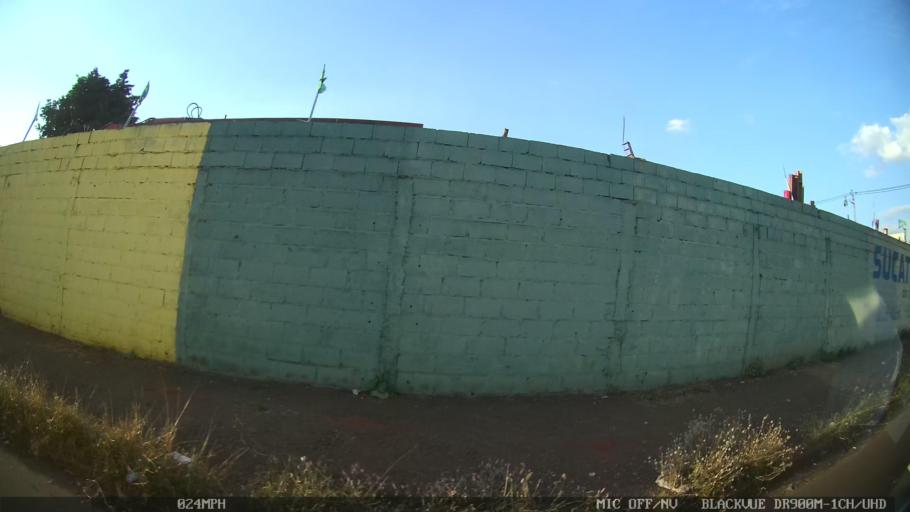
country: BR
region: Sao Paulo
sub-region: Ribeirao Preto
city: Ribeirao Preto
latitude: -21.1439
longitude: -47.7867
